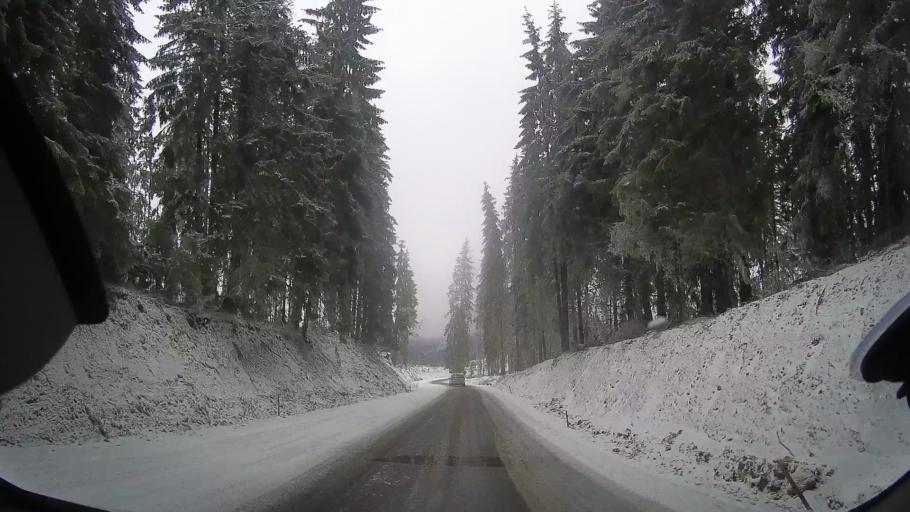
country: RO
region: Cluj
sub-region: Comuna Belis
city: Belis
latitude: 46.6389
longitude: 23.0414
